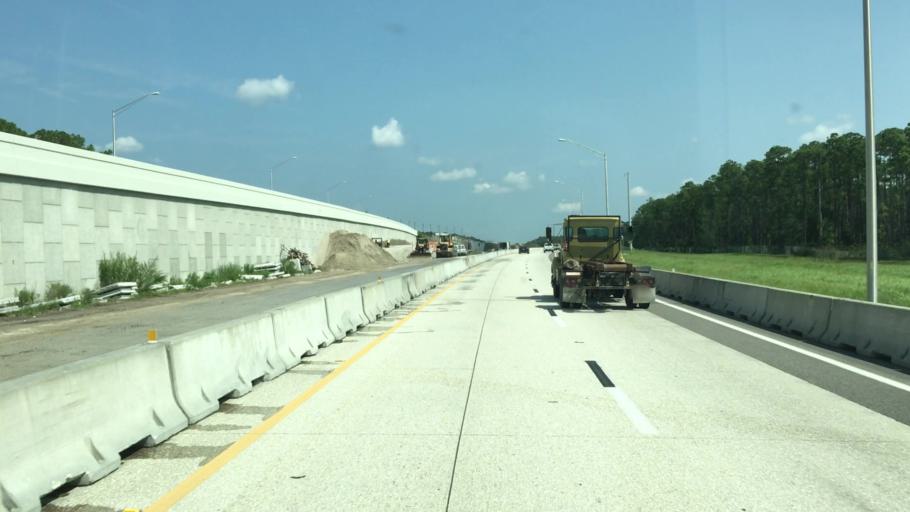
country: US
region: Florida
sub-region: Saint Johns County
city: Palm Valley
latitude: 30.1761
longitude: -81.5135
